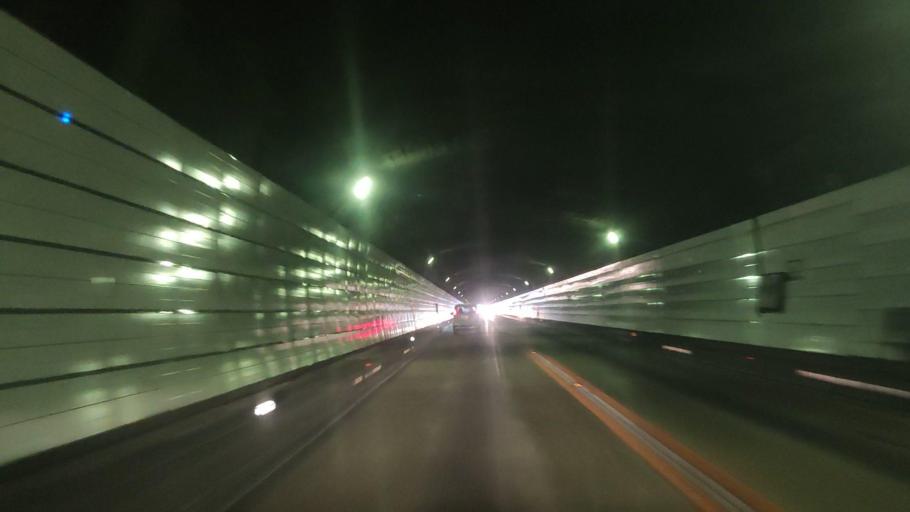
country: JP
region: Kumamoto
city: Hitoyoshi
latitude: 32.0946
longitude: 130.8028
